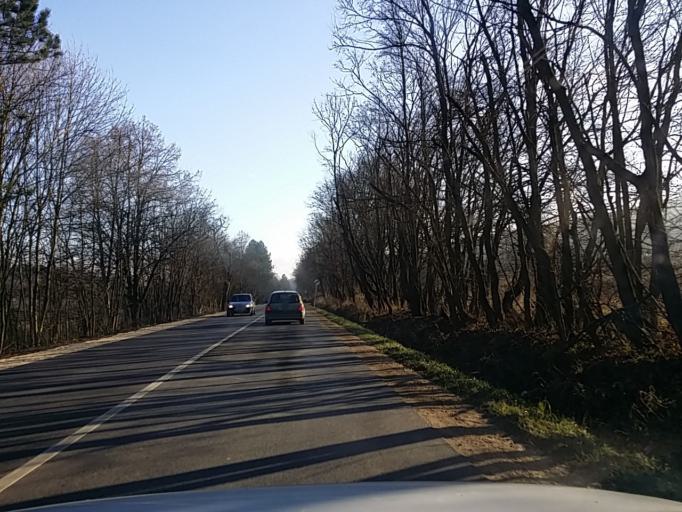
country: HU
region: Pest
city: Solymar
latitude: 47.5656
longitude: 18.9121
